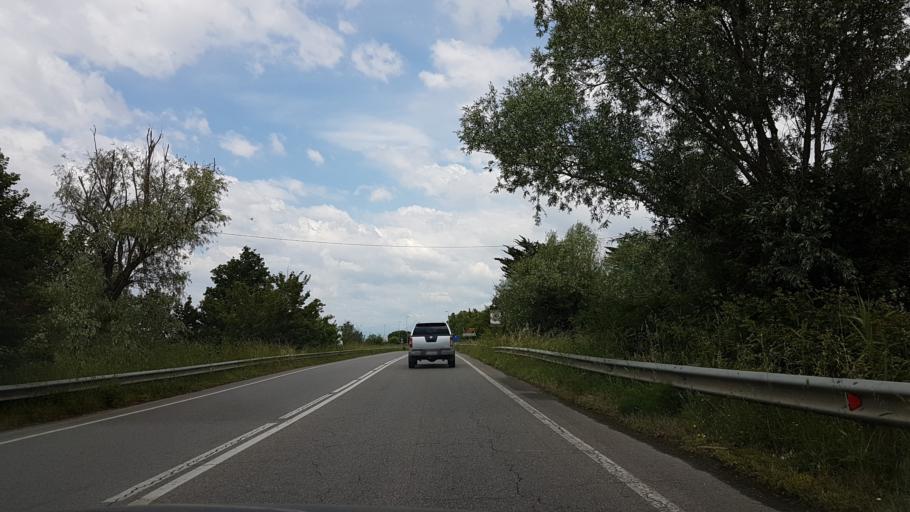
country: IT
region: Tuscany
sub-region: Provincia di Livorno
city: Vicarello
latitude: 43.6068
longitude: 10.4741
